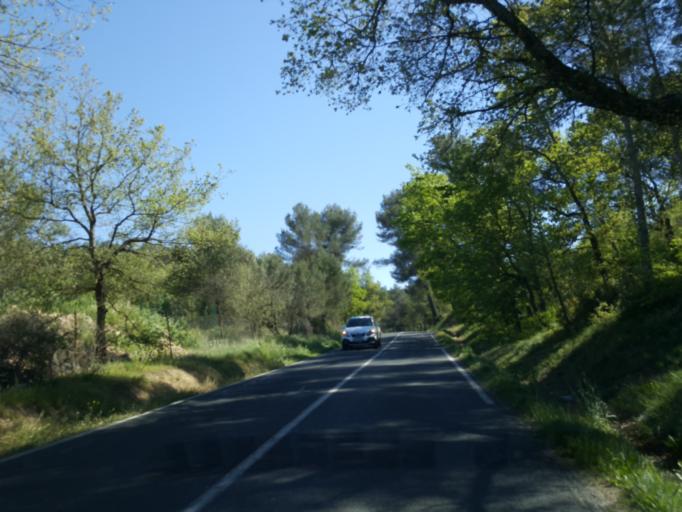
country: FR
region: Provence-Alpes-Cote d'Azur
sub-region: Departement des Bouches-du-Rhone
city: Cabries
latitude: 43.4380
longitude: 5.3625
